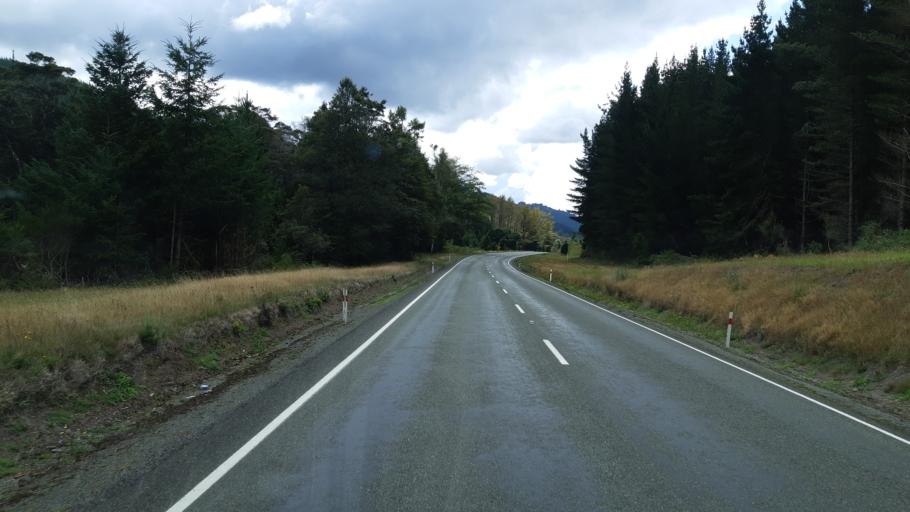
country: NZ
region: Tasman
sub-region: Tasman District
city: Wakefield
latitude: -41.5897
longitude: 172.7644
